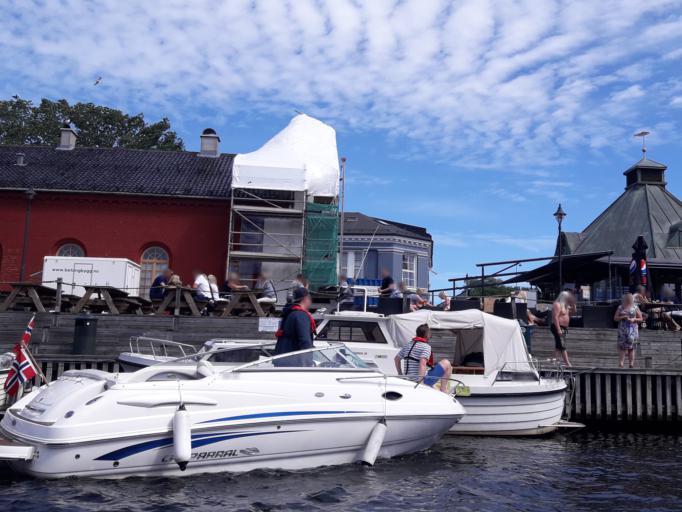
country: NO
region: Ostfold
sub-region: Moss
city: Moss
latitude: 59.4342
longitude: 10.6525
